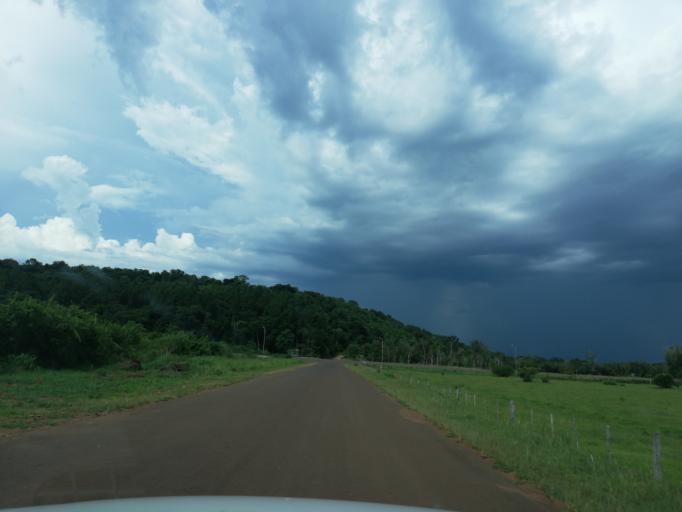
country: AR
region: Misiones
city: Cerro Azul
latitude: -27.5713
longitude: -55.4984
